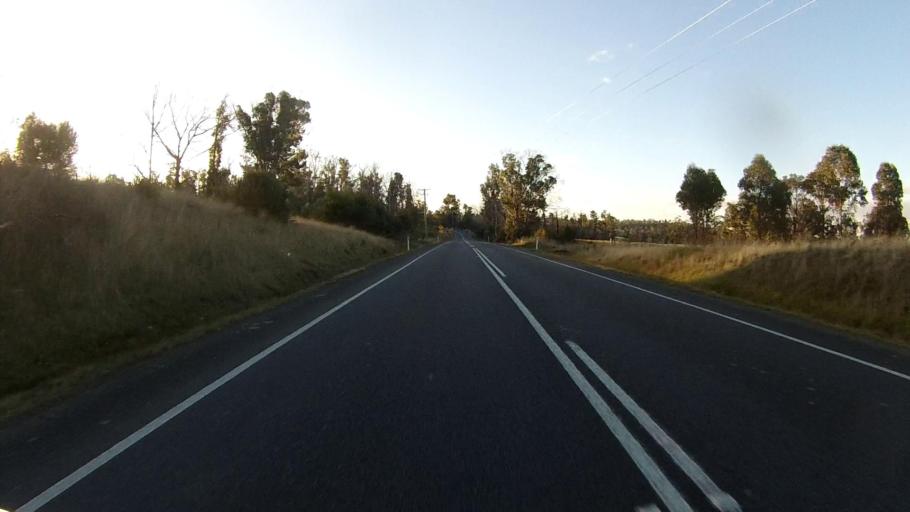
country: AU
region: Tasmania
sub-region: Sorell
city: Sorell
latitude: -42.8605
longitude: 147.8232
